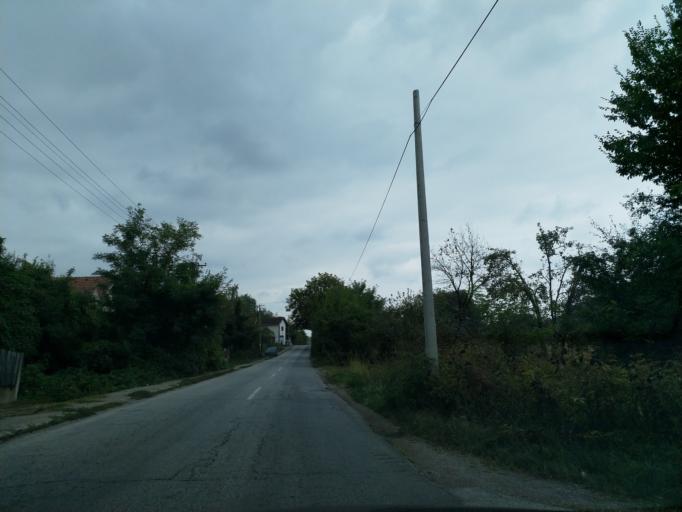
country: RS
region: Central Serbia
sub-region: Pomoravski Okrug
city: Jagodina
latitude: 44.0716
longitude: 21.1790
